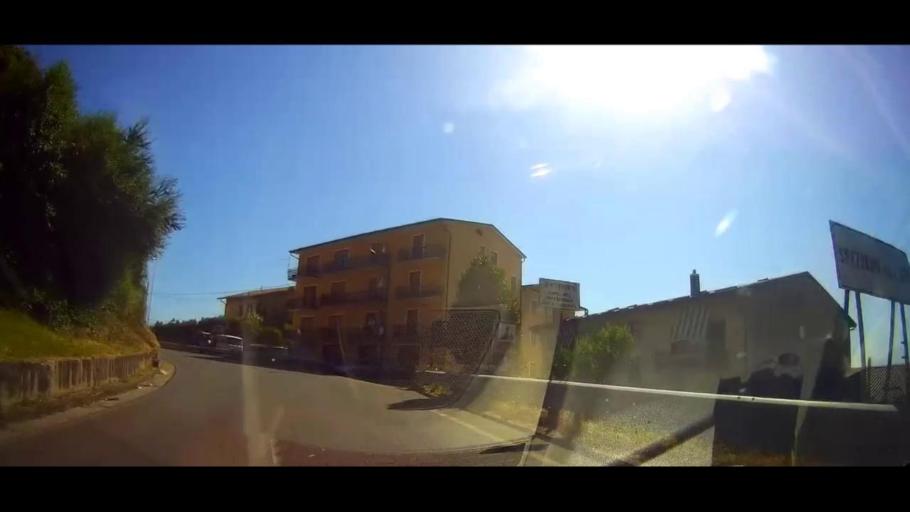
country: IT
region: Calabria
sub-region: Provincia di Cosenza
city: Celico
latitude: 39.3085
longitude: 16.3417
